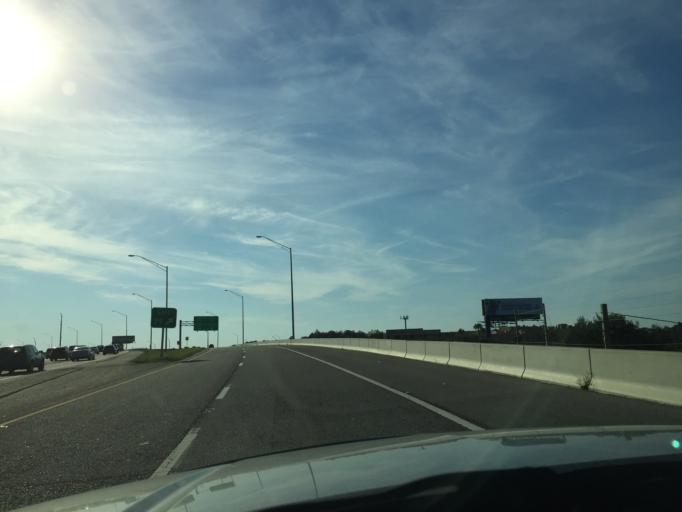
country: US
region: Florida
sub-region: Orange County
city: Holden Heights
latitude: 28.5097
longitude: -81.4157
